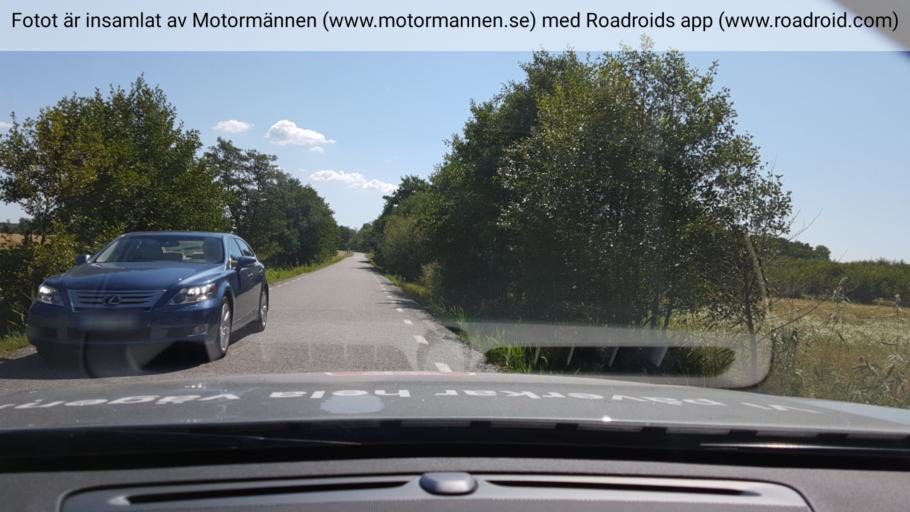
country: SE
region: Stockholm
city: Stenhamra
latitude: 59.4104
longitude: 17.6924
